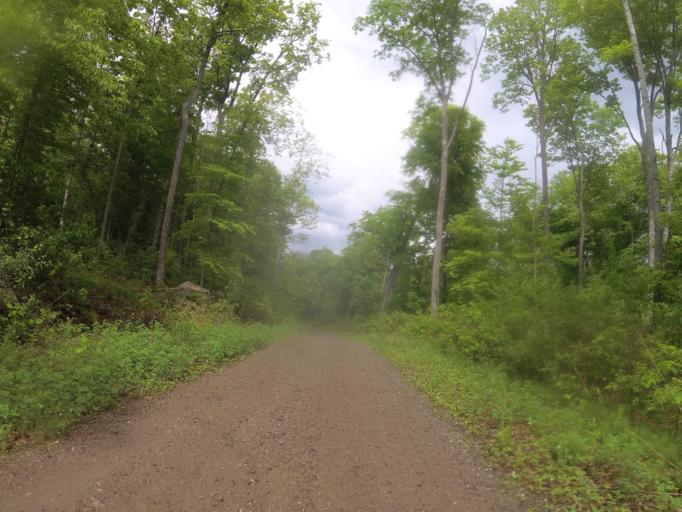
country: CA
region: Ontario
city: Renfrew
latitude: 45.1214
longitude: -76.8224
